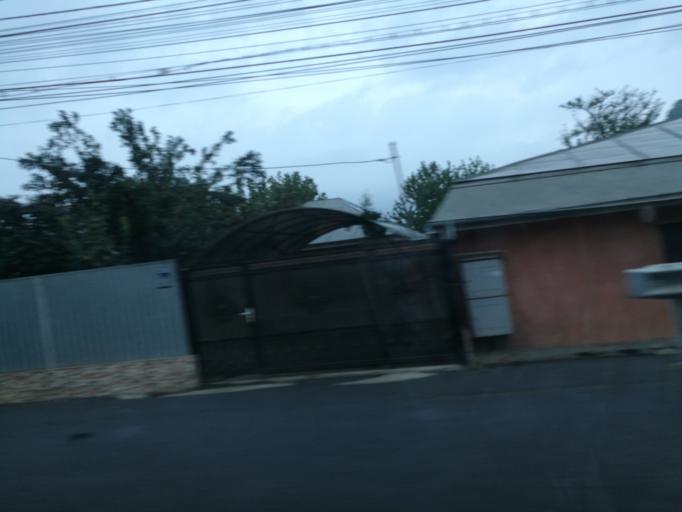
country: RO
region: Galati
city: Galati
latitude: 45.4680
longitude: 28.0344
